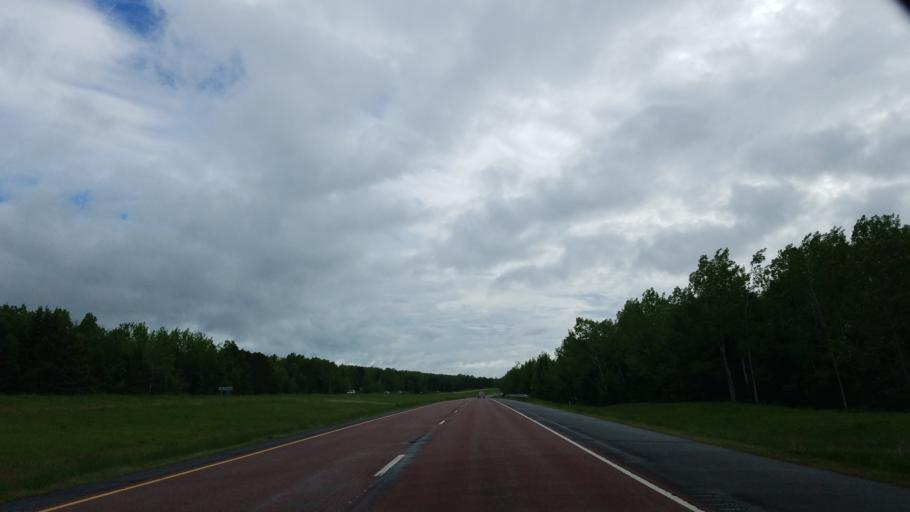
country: US
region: Minnesota
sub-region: Saint Louis County
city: Arnold
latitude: 46.9033
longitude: -91.8964
